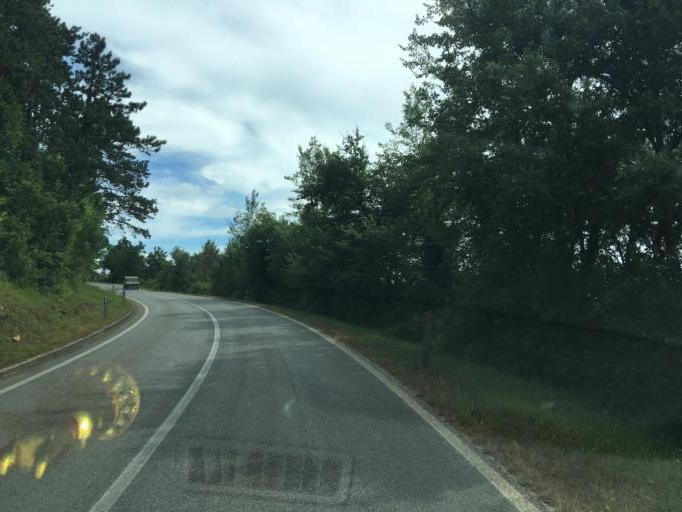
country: HR
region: Istarska
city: Karojba
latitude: 45.2844
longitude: 13.8339
